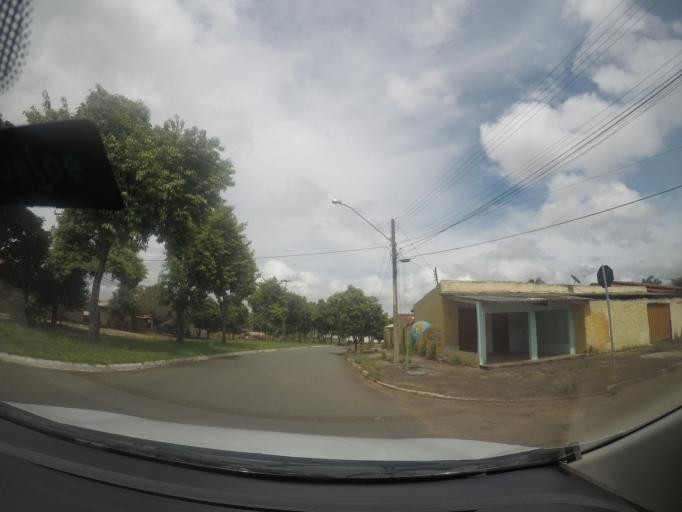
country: BR
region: Goias
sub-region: Goiania
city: Goiania
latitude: -16.7173
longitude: -49.3116
